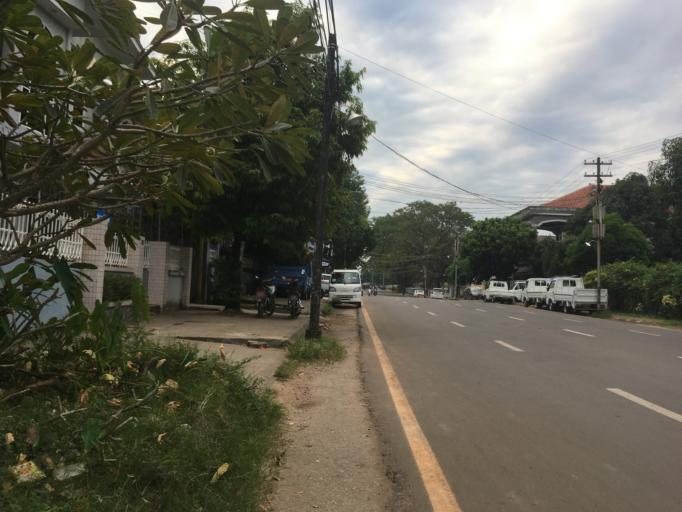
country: MM
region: Mon
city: Mawlamyine
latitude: 16.4701
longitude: 97.6226
